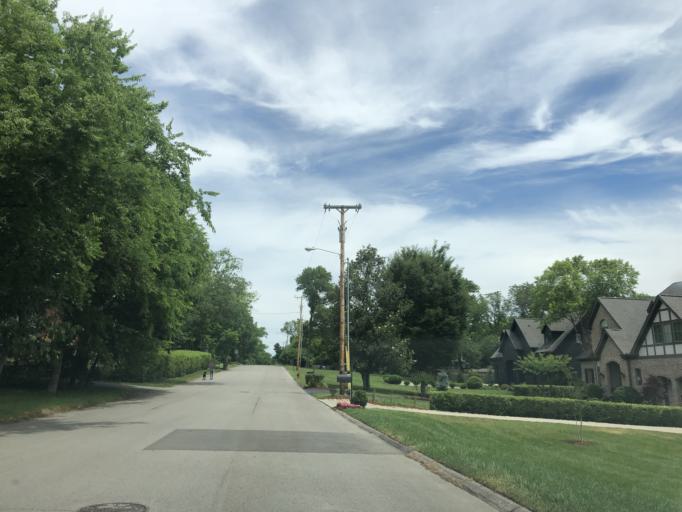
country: US
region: Tennessee
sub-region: Davidson County
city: Oak Hill
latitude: 36.1115
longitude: -86.8033
